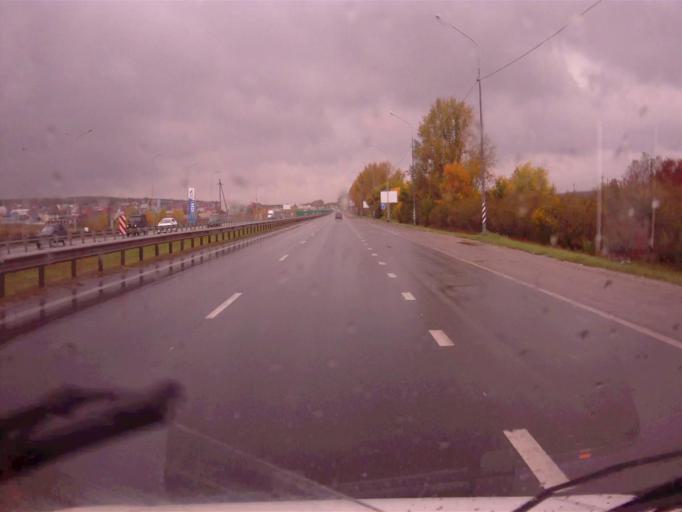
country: RU
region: Chelyabinsk
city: Dolgoderevenskoye
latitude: 55.2763
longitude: 61.3438
